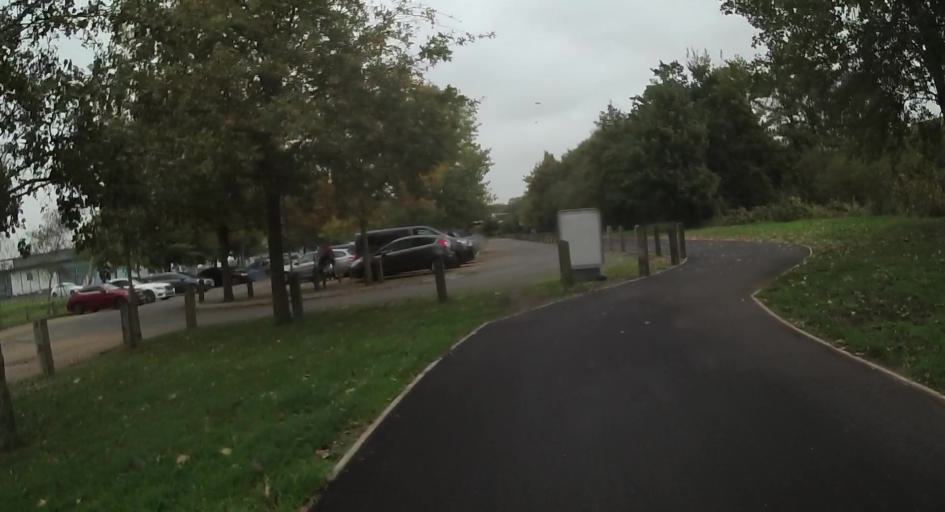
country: GB
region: England
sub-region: Surrey
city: Byfleet
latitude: 51.3522
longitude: -0.4663
